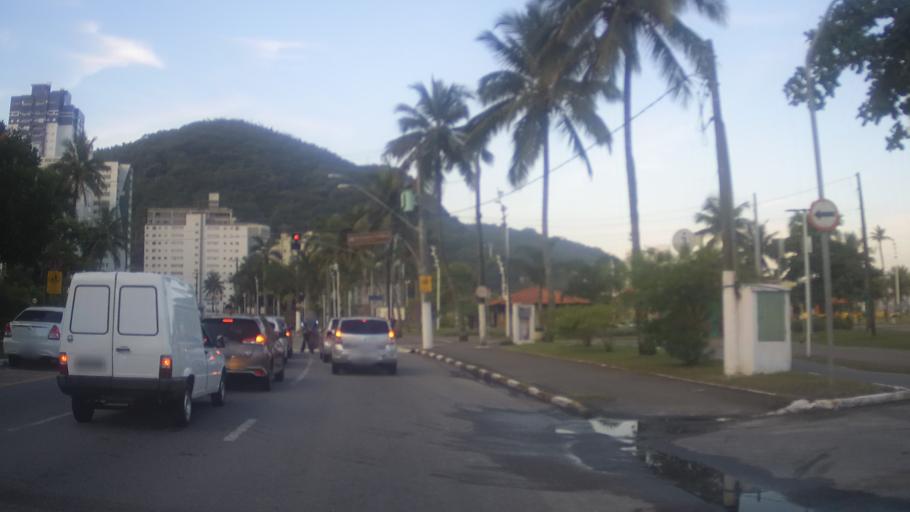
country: BR
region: Sao Paulo
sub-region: Sao Vicente
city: Sao Vicente
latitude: -23.9726
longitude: -46.3694
